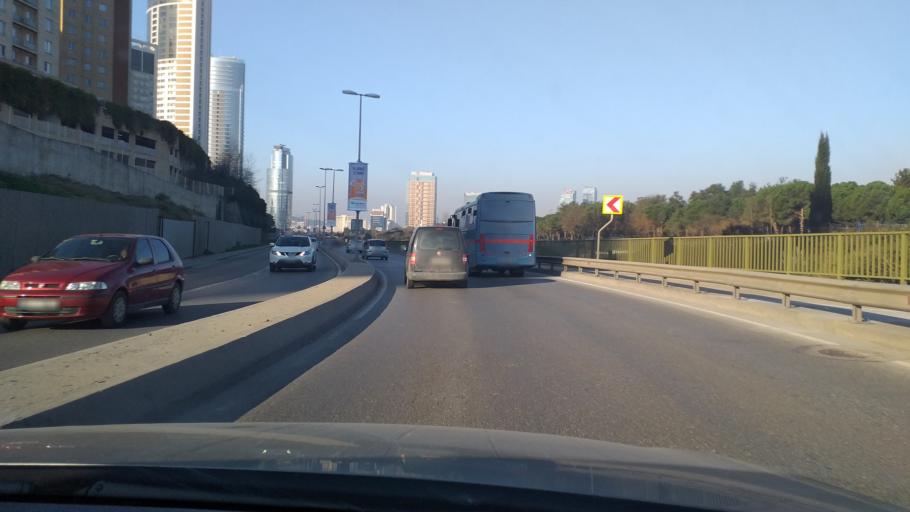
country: TR
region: Istanbul
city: Maltepe
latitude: 40.9215
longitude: 29.1833
